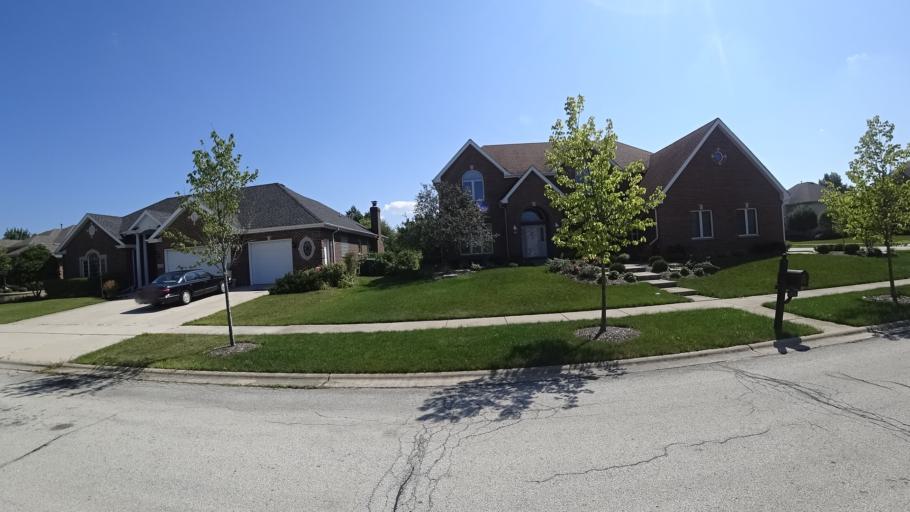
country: US
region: Illinois
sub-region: Cook County
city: Orland Park
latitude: 41.6336
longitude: -87.8301
